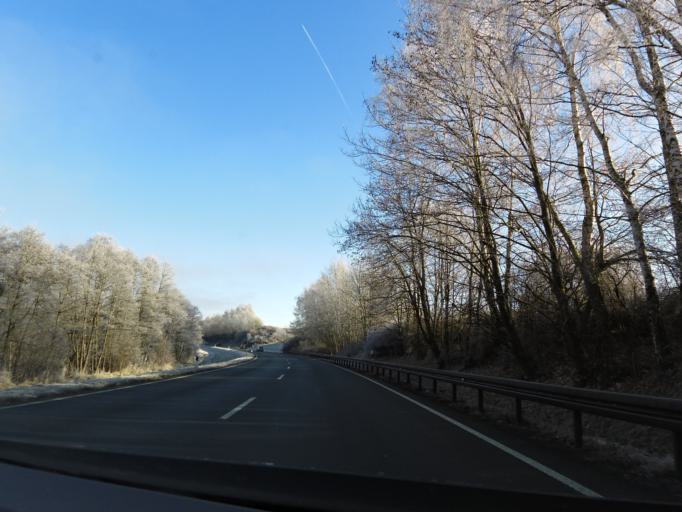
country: DE
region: Bavaria
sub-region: Upper Franconia
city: Thiersheim
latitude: 50.0239
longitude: 12.1402
